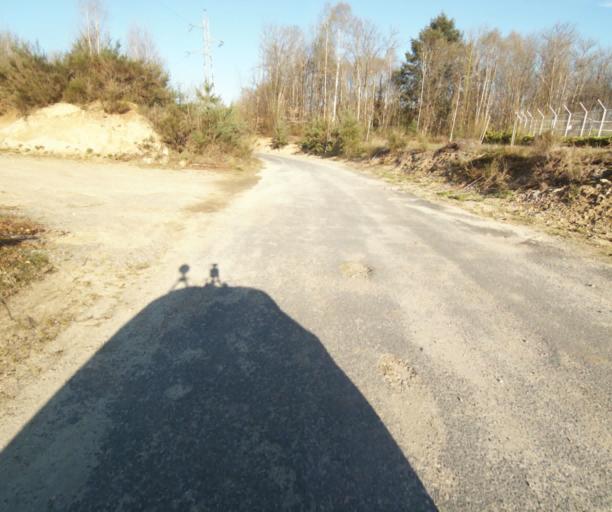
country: FR
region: Limousin
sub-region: Departement de la Correze
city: Correze
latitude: 45.3383
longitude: 1.9031
